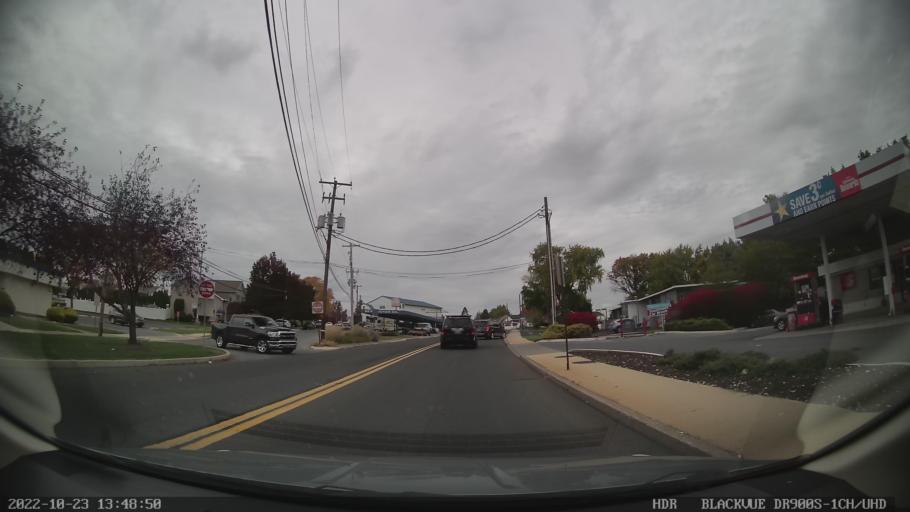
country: US
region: Pennsylvania
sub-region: Lehigh County
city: Fullerton
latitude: 40.6431
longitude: -75.4738
